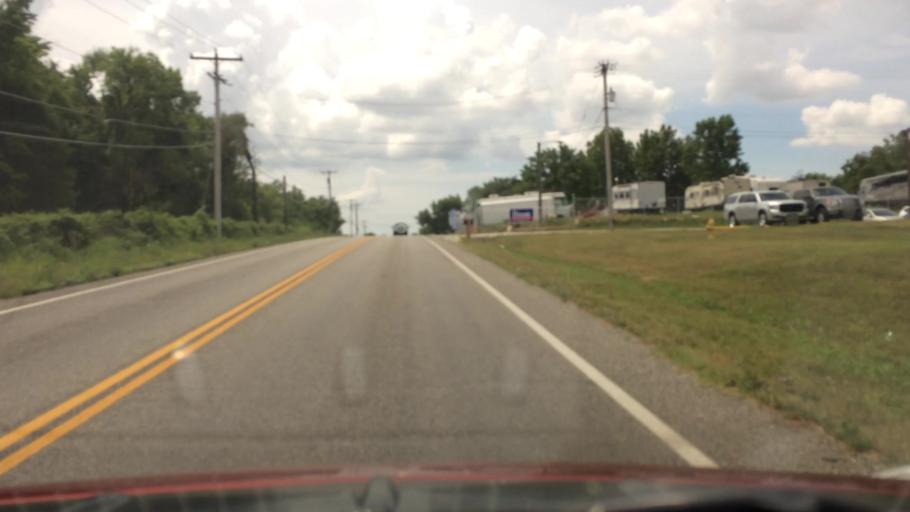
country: US
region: Missouri
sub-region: Greene County
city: Springfield
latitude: 37.2715
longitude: -93.2646
